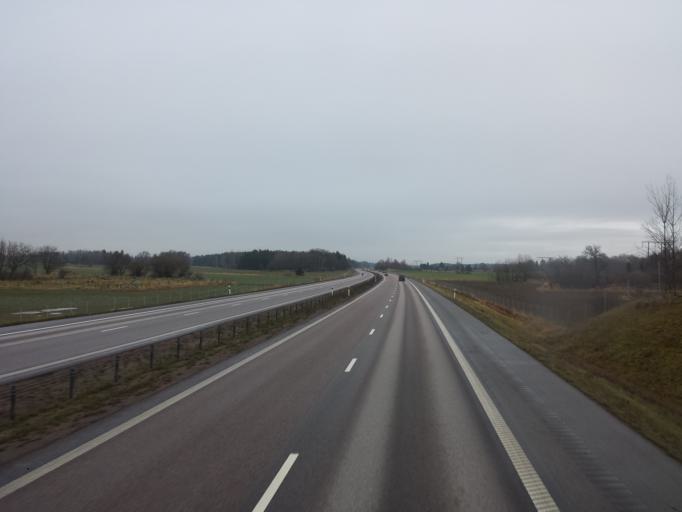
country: SE
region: OEstergoetland
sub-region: Linkopings Kommun
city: Linghem
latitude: 58.4584
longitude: 15.7851
